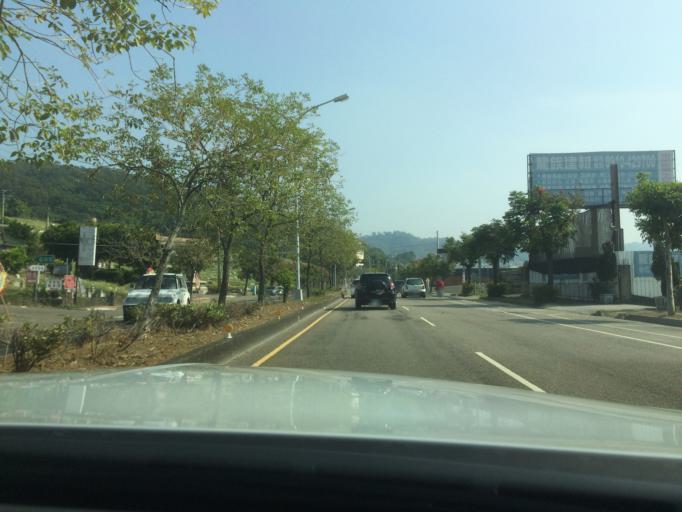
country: TW
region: Taiwan
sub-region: Taichung City
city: Taichung
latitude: 24.1810
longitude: 120.7247
